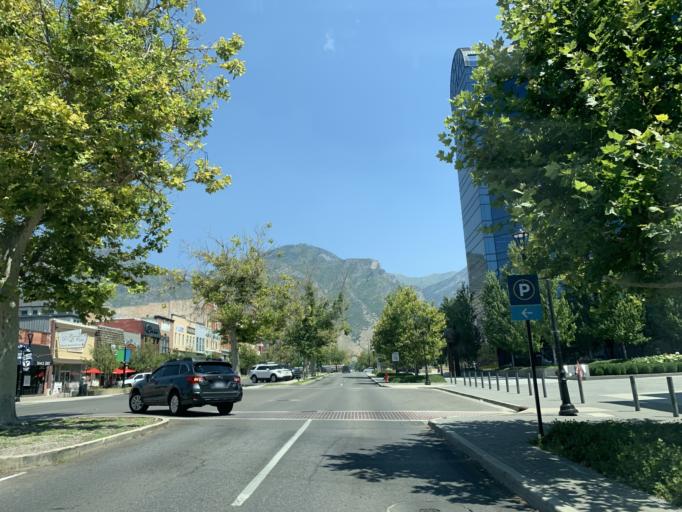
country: US
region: Utah
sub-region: Utah County
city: Provo
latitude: 40.2337
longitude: -111.6608
